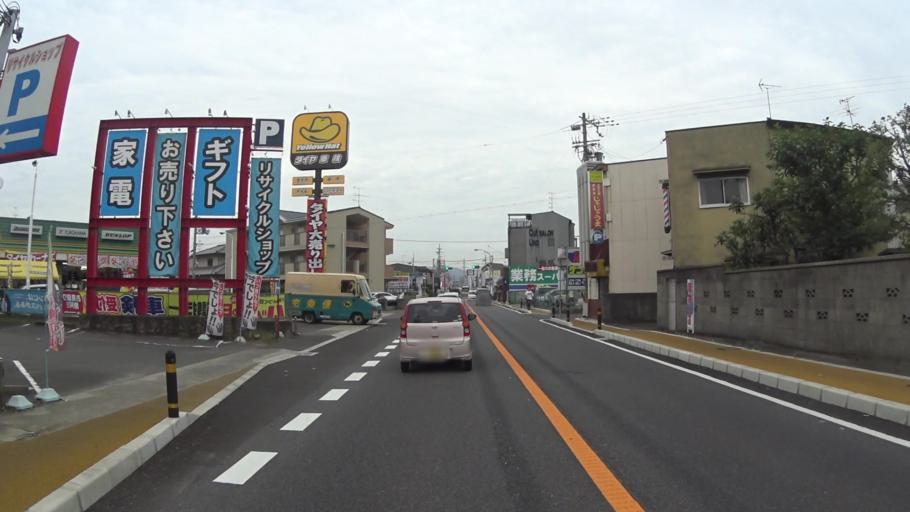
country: JP
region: Kyoto
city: Tanabe
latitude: 34.8561
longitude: 135.7777
